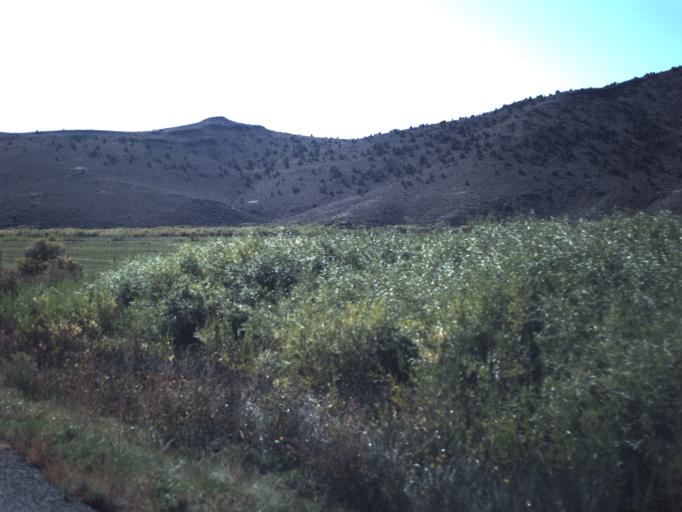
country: US
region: Utah
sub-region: Piute County
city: Junction
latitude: 38.1664
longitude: -112.0368
